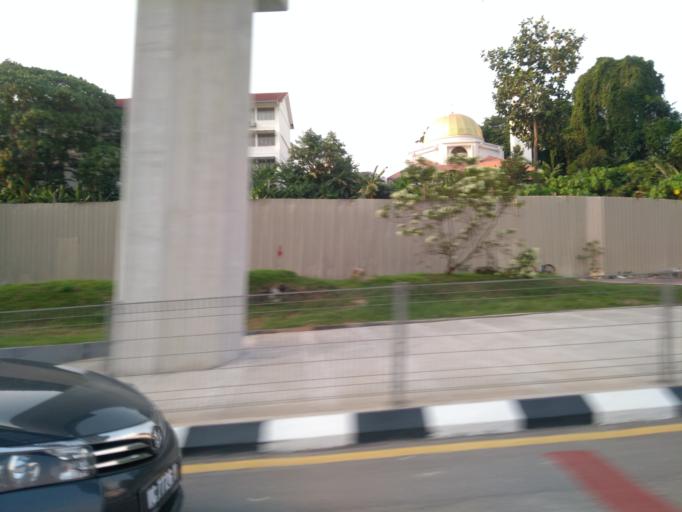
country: MY
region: Kuala Lumpur
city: Kuala Lumpur
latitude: 3.1373
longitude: 101.7019
